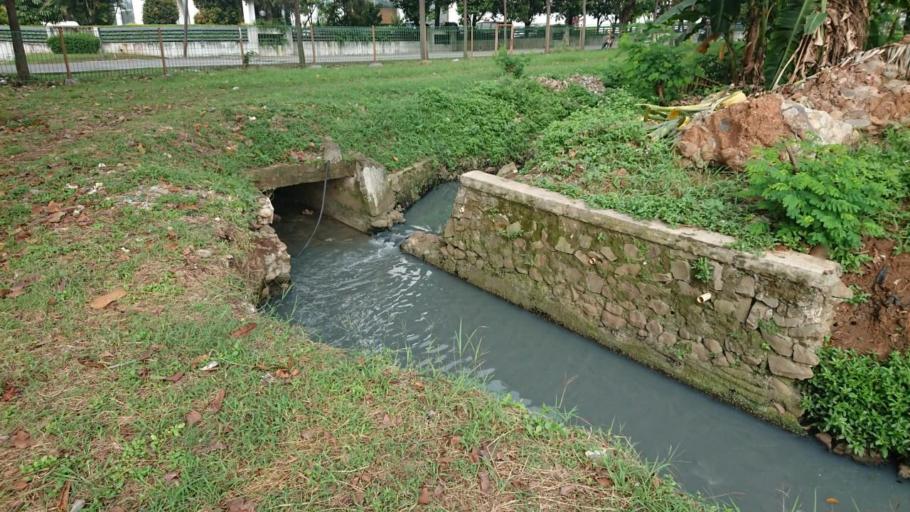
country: ID
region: Jakarta Raya
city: Jakarta
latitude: -6.2026
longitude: 106.9114
